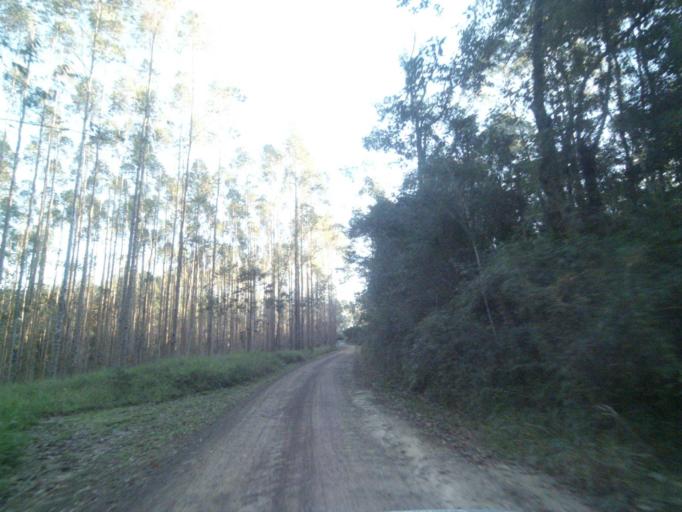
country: BR
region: Parana
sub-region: Telemaco Borba
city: Telemaco Borba
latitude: -24.4946
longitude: -50.5998
